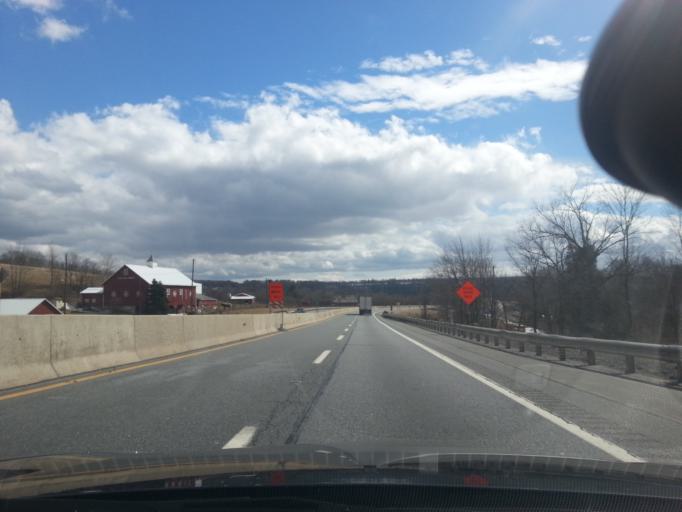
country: US
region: Pennsylvania
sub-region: Carbon County
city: Weissport East
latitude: 40.8630
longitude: -75.6509
